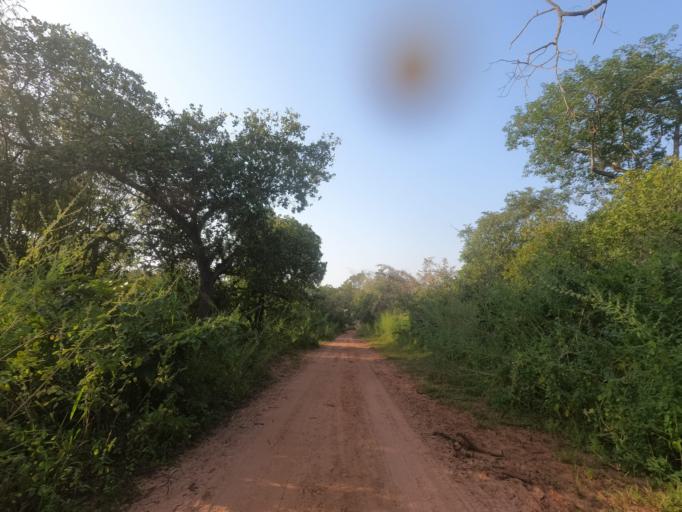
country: GW
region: Oio
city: Bissora
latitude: 12.3778
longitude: -15.7121
